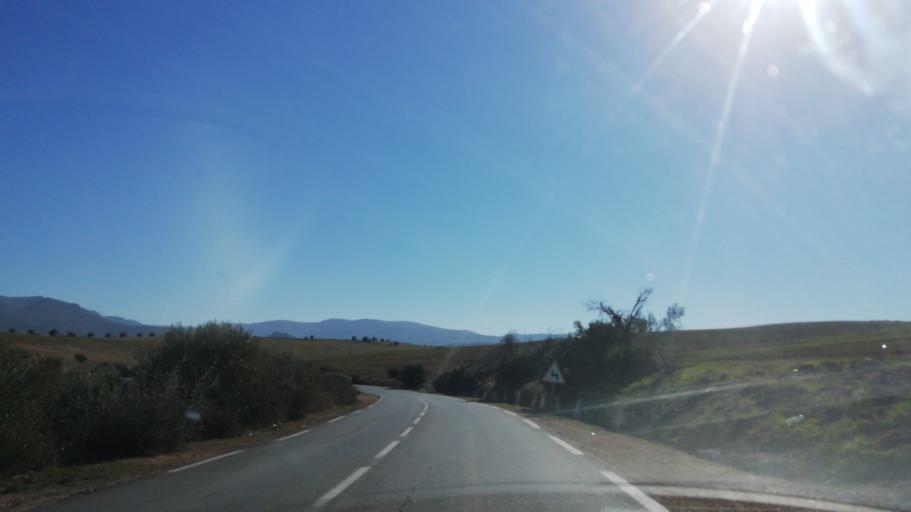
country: DZ
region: Tlemcen
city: Beni Mester
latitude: 34.8264
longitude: -1.5863
